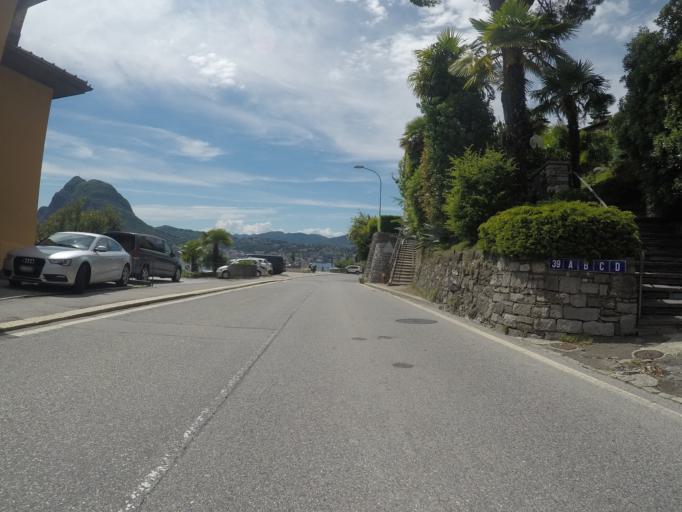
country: CH
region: Ticino
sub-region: Lugano District
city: Viganello
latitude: 46.0016
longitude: 8.9805
